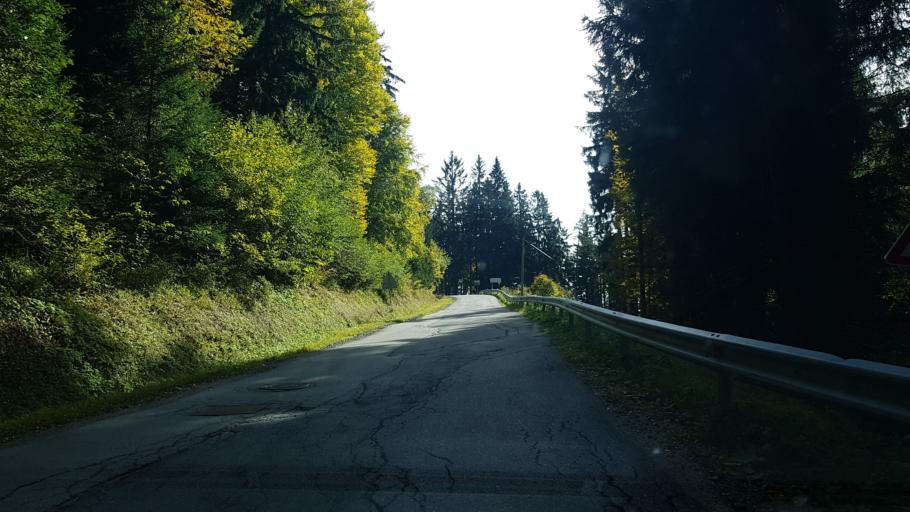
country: SI
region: Slovenj Gradec
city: Legen
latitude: 46.4986
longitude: 15.1977
